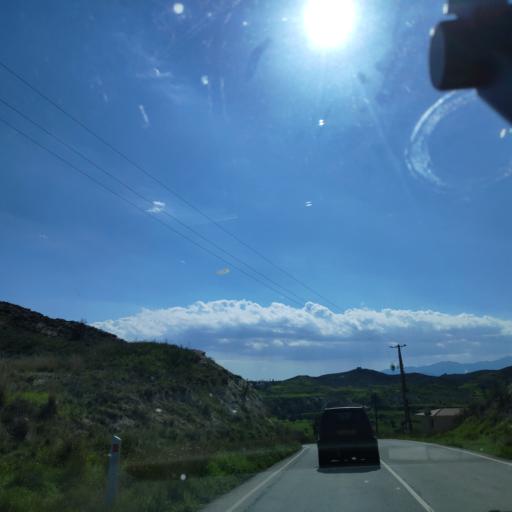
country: CY
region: Lefkosia
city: Tseri
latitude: 35.0301
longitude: 33.3279
